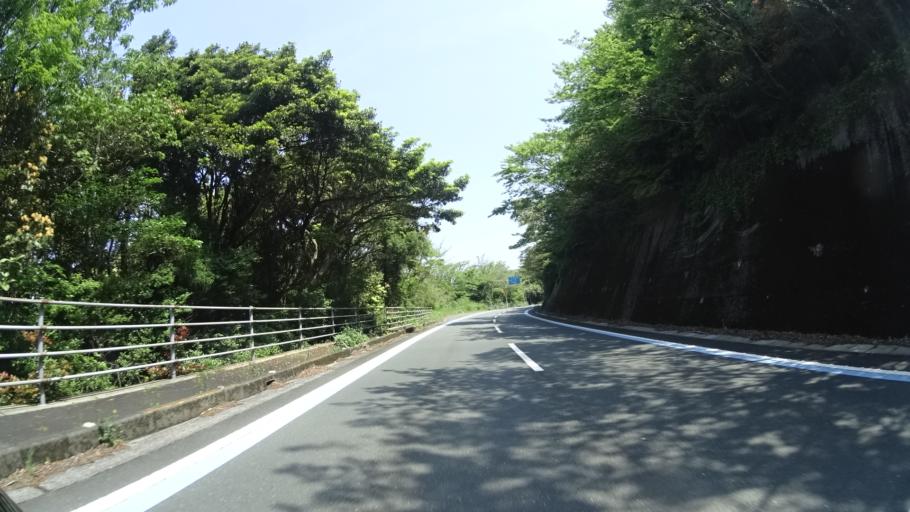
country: JP
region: Ehime
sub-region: Nishiuwa-gun
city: Ikata-cho
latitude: 33.4137
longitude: 132.1725
